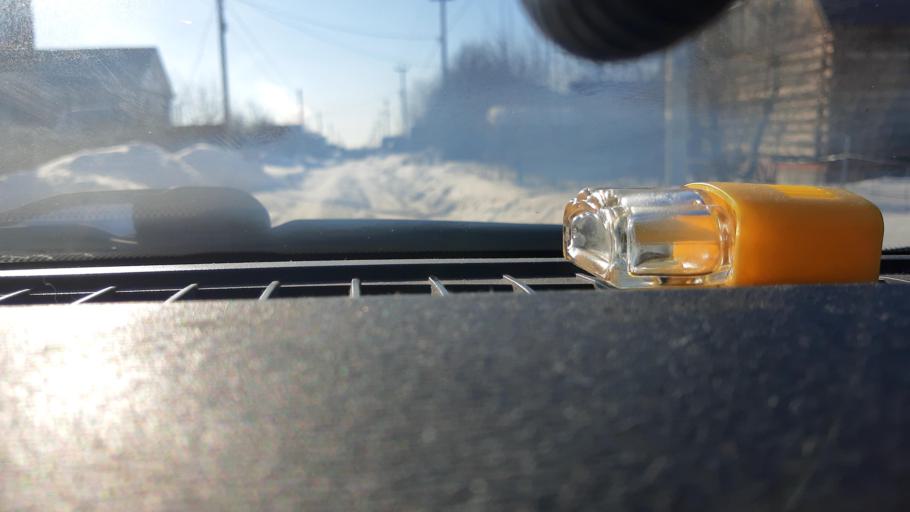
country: RU
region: Bashkortostan
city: Iglino
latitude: 54.7809
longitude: 56.2496
